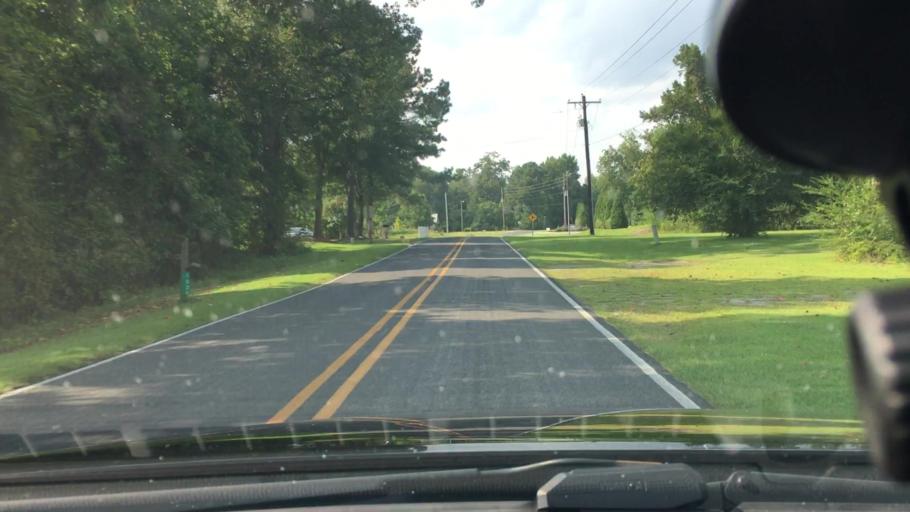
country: US
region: North Carolina
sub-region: Craven County
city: New Bern
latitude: 35.1825
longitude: -77.0574
